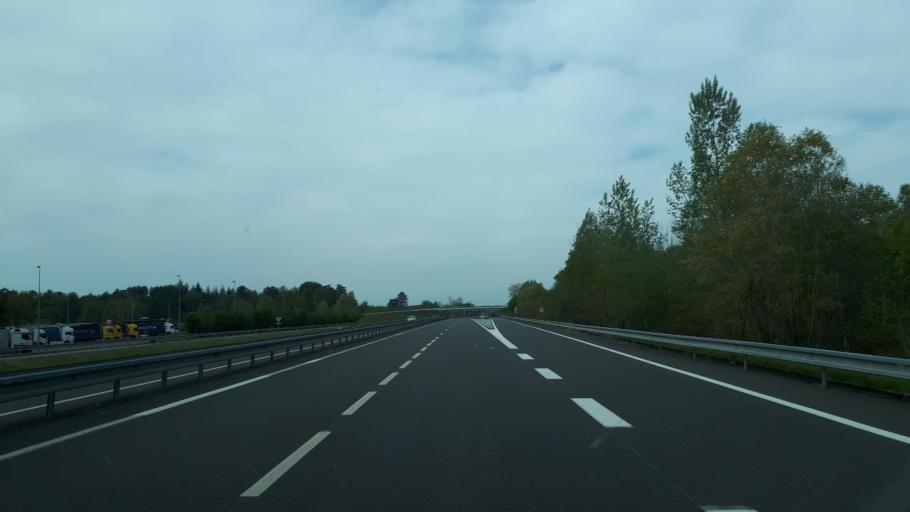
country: FR
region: Centre
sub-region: Departement du Loir-et-Cher
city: Pruniers-en-Sologne
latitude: 47.3400
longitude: 1.6689
